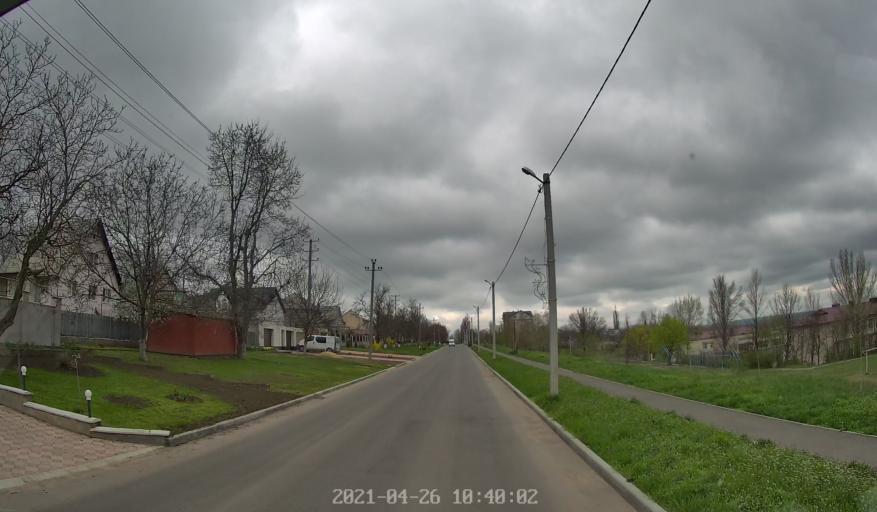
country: MD
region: Chisinau
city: Cricova
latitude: 47.1324
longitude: 28.8608
